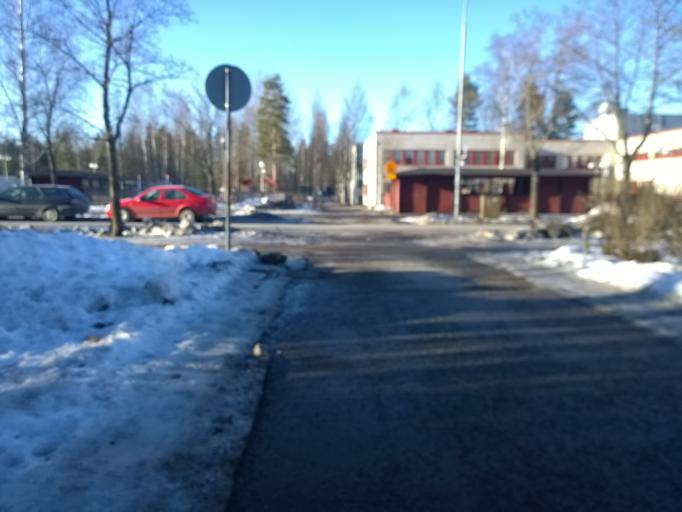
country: FI
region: Pirkanmaa
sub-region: Tampere
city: Tampere
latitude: 61.4461
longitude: 23.8314
